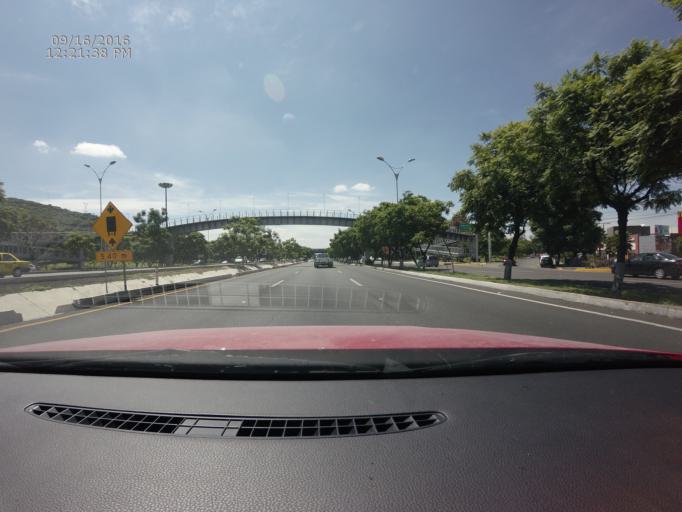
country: MX
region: Queretaro
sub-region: Queretaro
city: Sergio Villasenor
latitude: 20.6475
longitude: -100.4313
